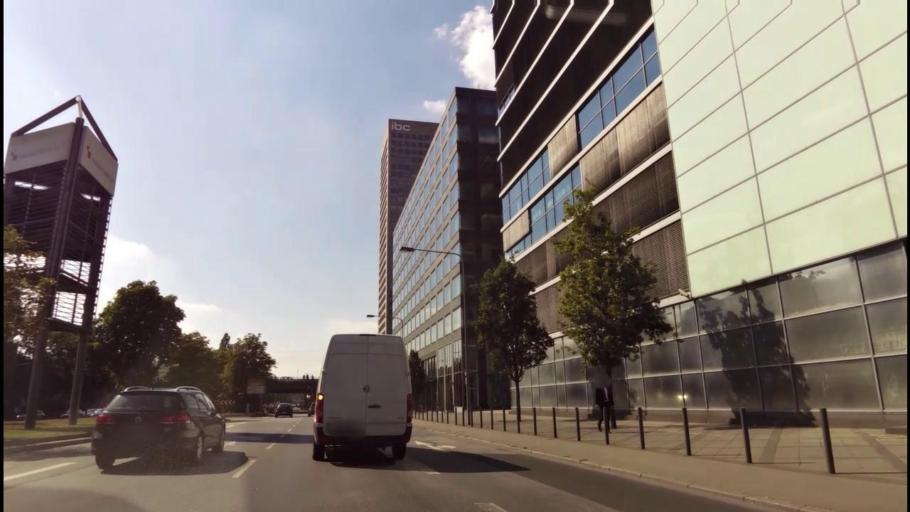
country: DE
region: Hesse
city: Niederrad
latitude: 50.1141
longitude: 8.6453
